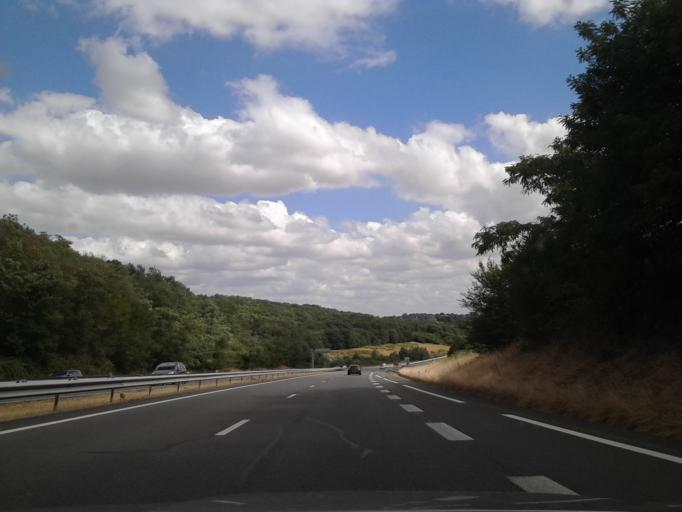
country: FR
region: Centre
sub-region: Departement du Cher
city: Orval
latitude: 46.7485
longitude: 2.4228
